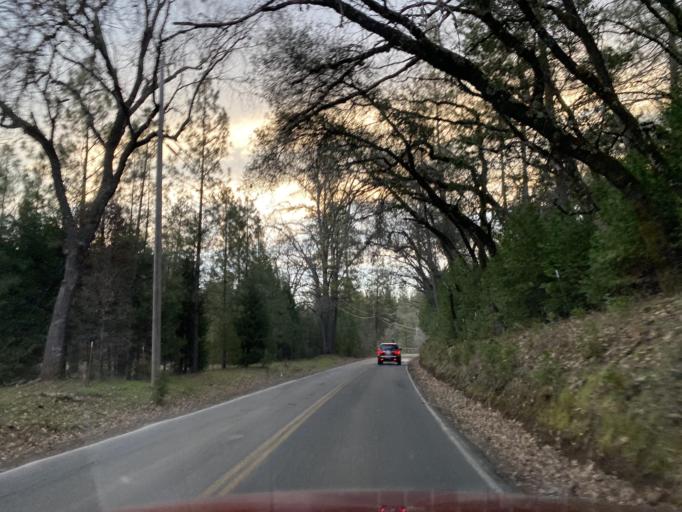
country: US
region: California
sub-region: Amador County
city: Pine Grove
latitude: 38.4974
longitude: -120.7303
